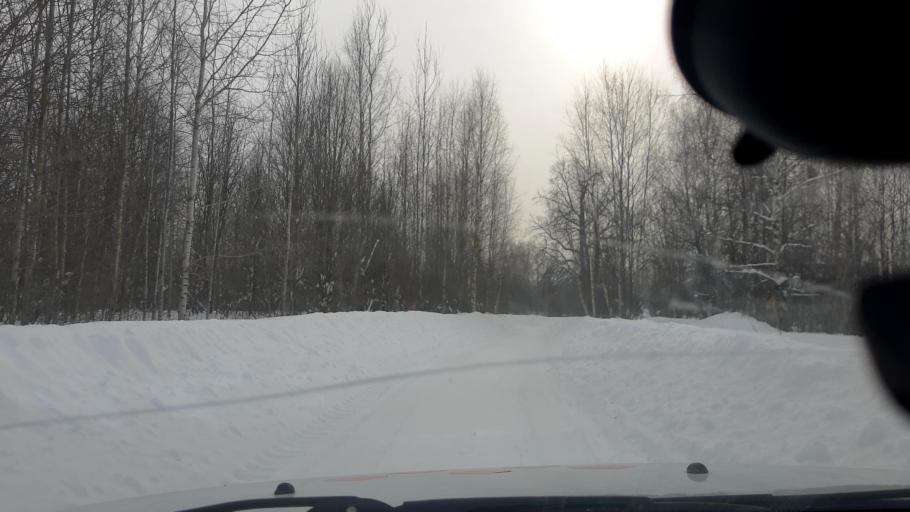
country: RU
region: Nizjnij Novgorod
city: Lukino
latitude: 56.5328
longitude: 43.7707
